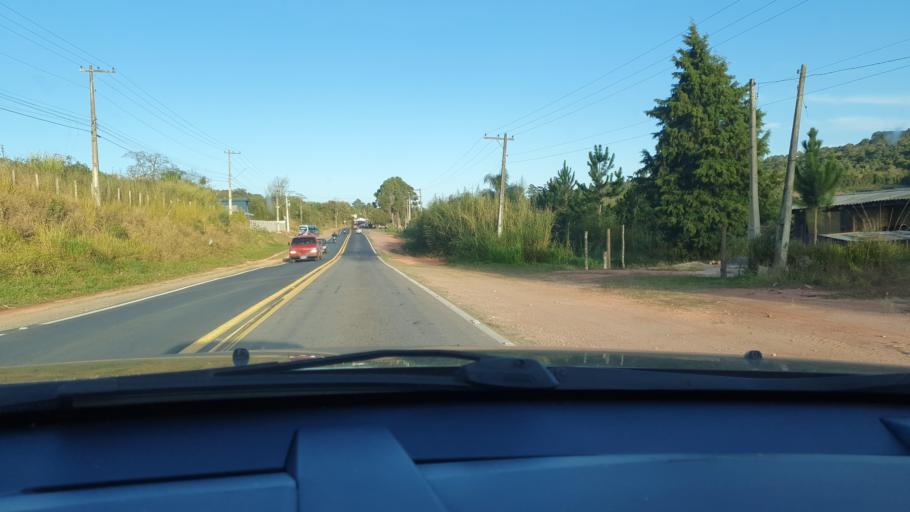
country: BR
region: Sao Paulo
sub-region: Ibiuna
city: Ibiuna
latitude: -23.6759
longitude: -47.3196
